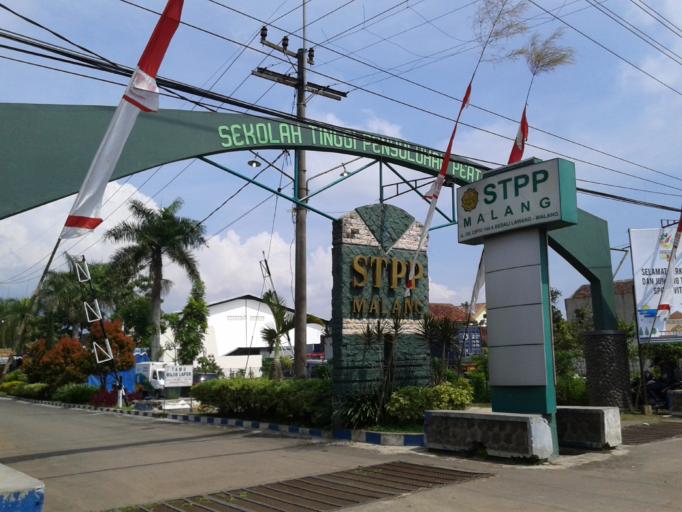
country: ID
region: East Java
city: Lawang
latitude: -7.8642
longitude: 112.6842
